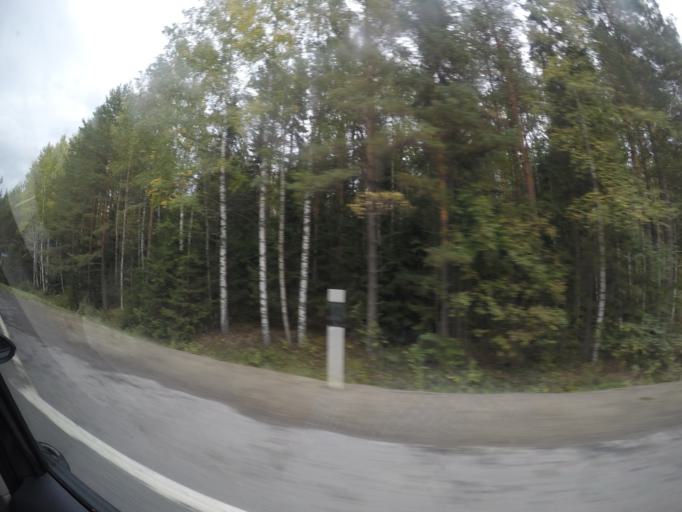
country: FI
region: Haeme
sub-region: Haemeenlinna
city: Parola
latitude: 61.1506
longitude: 24.4122
